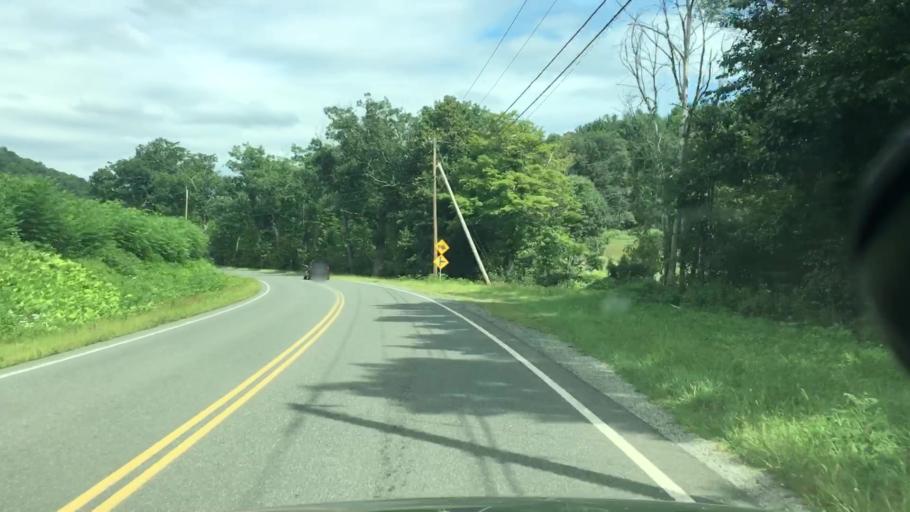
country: US
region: Massachusetts
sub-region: Franklin County
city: Colrain
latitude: 42.6877
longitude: -72.6909
